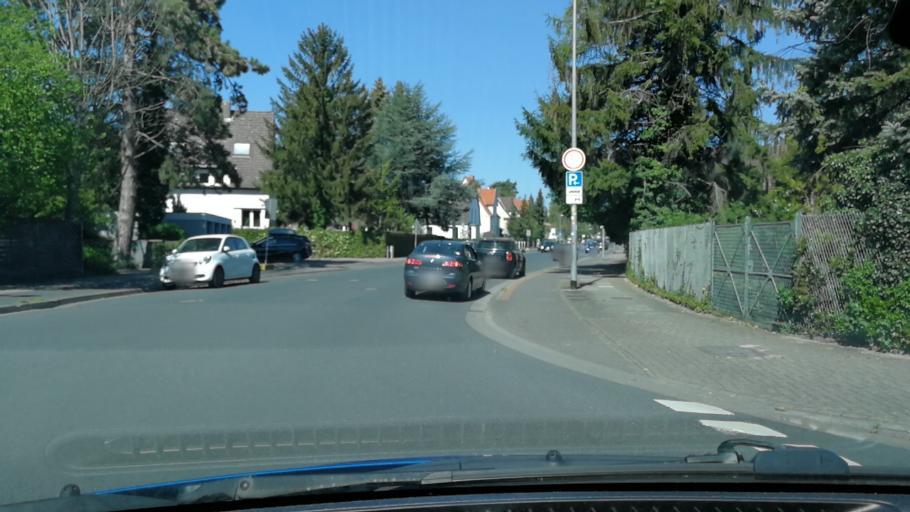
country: DE
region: Lower Saxony
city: Laatzen
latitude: 52.3562
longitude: 9.8194
